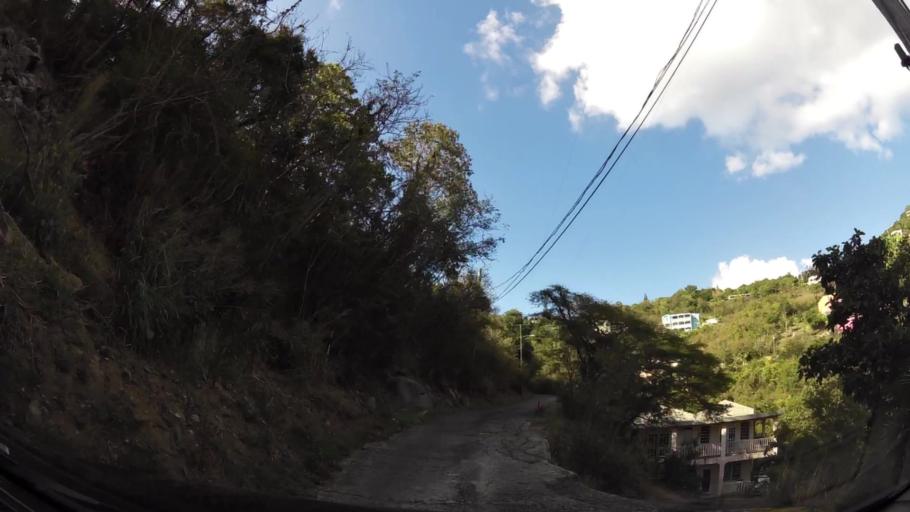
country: VG
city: Road Town
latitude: 18.3930
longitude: -64.6775
